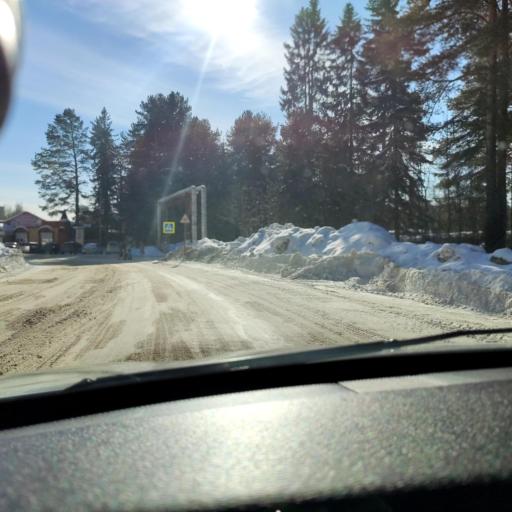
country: RU
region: Perm
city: Dobryanka
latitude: 58.4708
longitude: 56.3944
